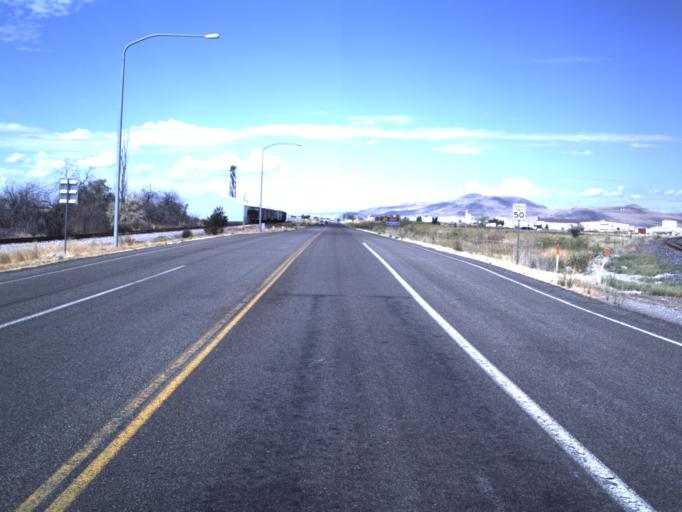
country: US
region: Utah
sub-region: Box Elder County
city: Honeyville
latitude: 41.5523
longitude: -112.1157
